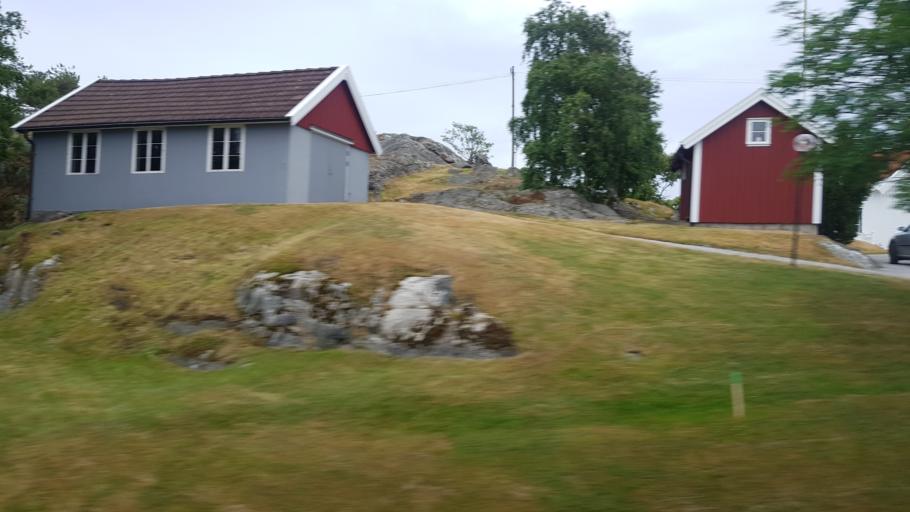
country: SE
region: Vaestra Goetaland
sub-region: Tjorns Kommun
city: Skaerhamn
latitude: 57.9850
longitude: 11.5693
